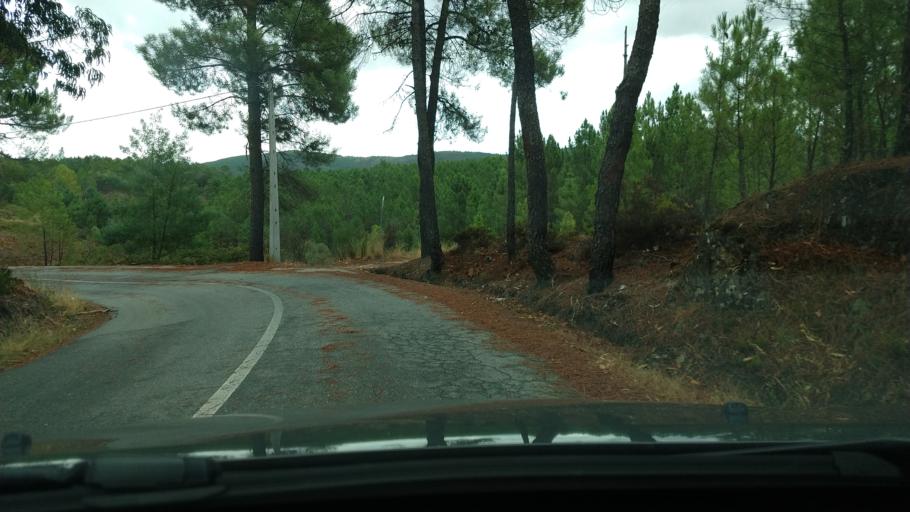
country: PT
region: Castelo Branco
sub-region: Concelho do Fundao
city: Aldeia de Joanes
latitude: 40.2209
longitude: -7.6370
